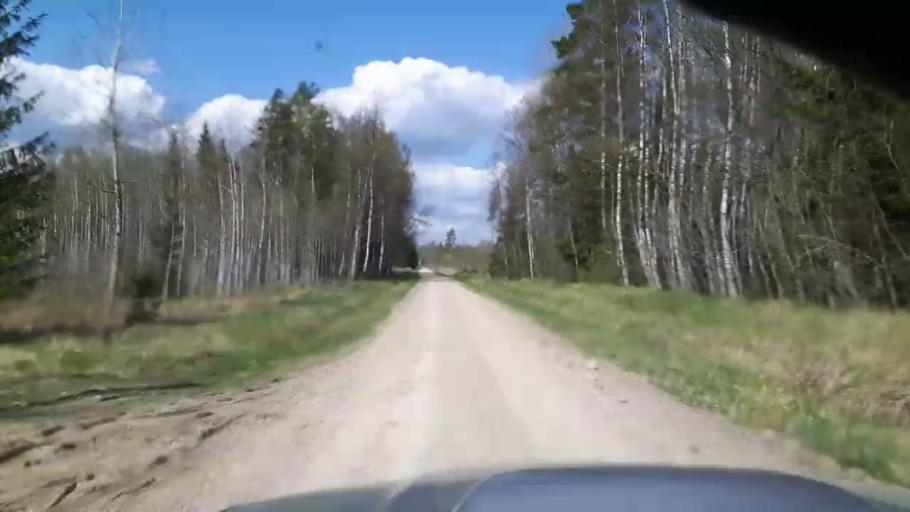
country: EE
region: Paernumaa
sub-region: Tootsi vald
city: Tootsi
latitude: 58.4491
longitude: 24.9008
